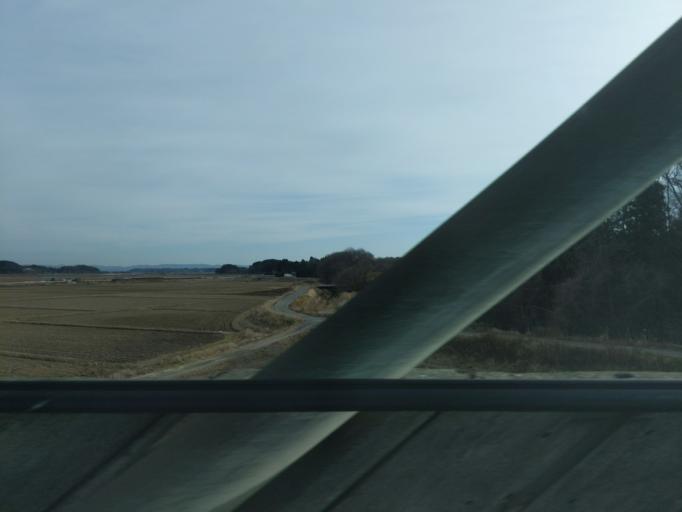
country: JP
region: Miyagi
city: Kogota
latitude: 38.7235
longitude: 141.0574
